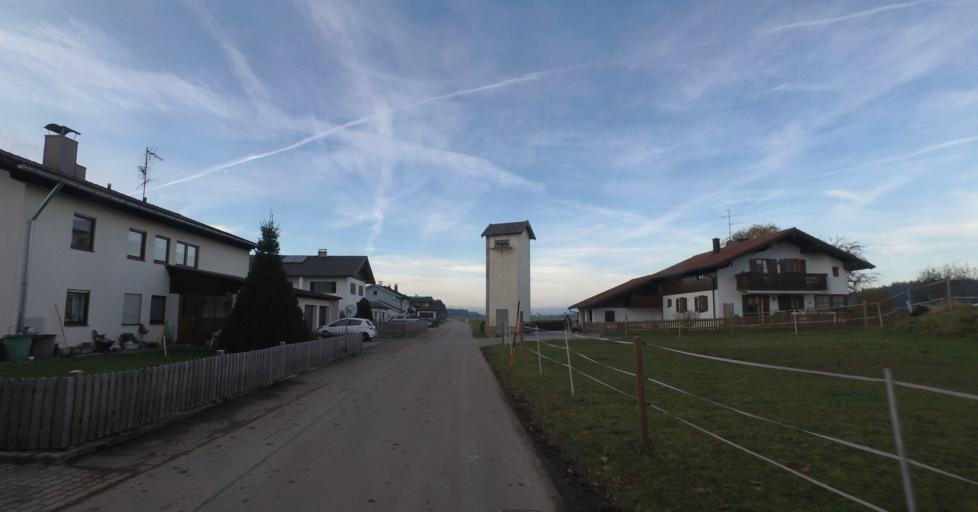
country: DE
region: Bavaria
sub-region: Upper Bavaria
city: Nussdorf
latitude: 47.8884
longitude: 12.6093
